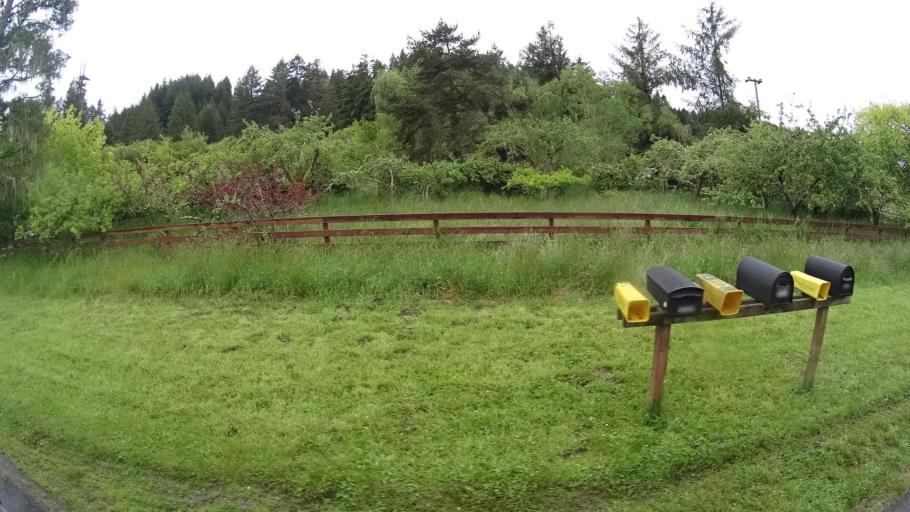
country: US
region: California
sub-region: Humboldt County
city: Bayside
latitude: 40.8325
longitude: -124.0431
